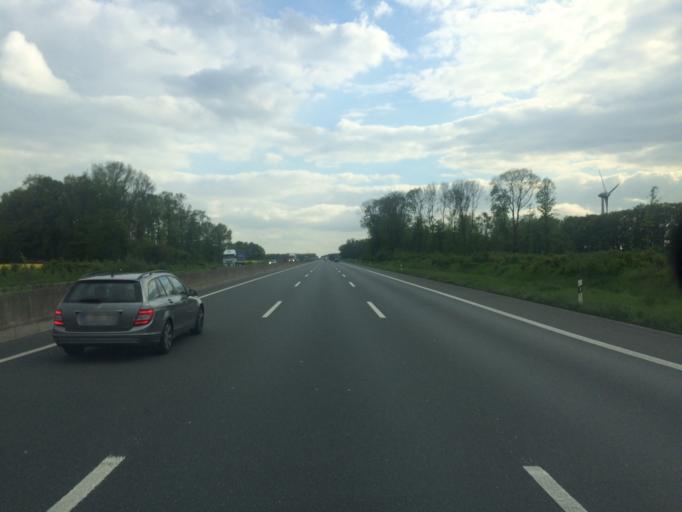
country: DE
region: North Rhine-Westphalia
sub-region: Regierungsbezirk Munster
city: Beckum
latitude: 51.7459
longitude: 7.9929
